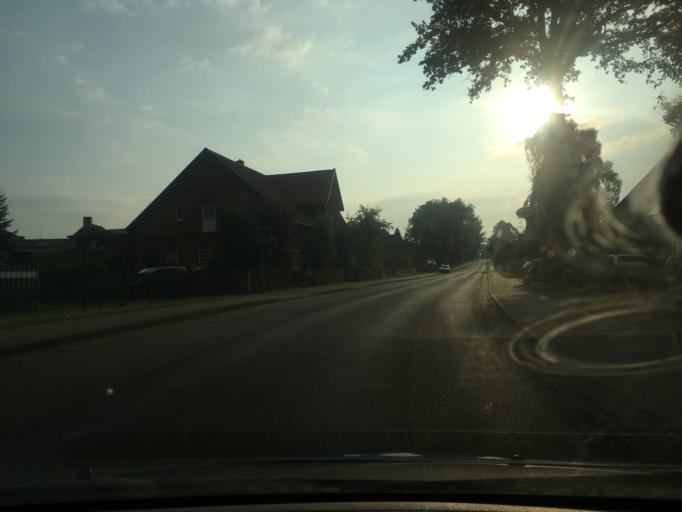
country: DE
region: Lower Saxony
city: Eyendorf
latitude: 53.2056
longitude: 10.1584
